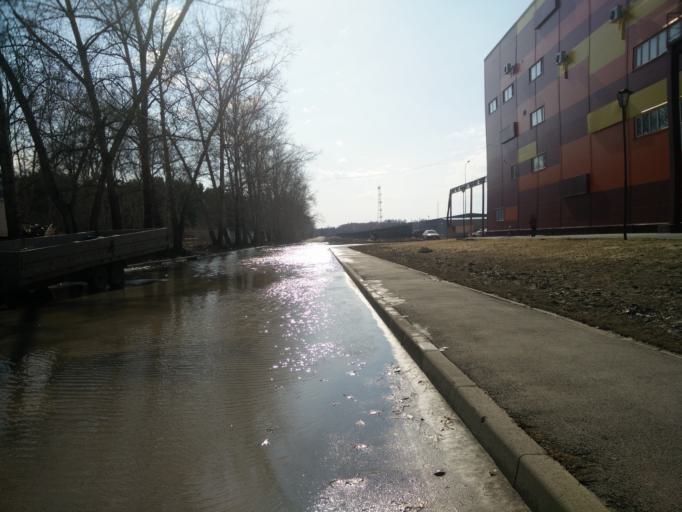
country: RU
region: Novosibirsk
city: Berdsk
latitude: 54.7648
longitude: 83.0810
